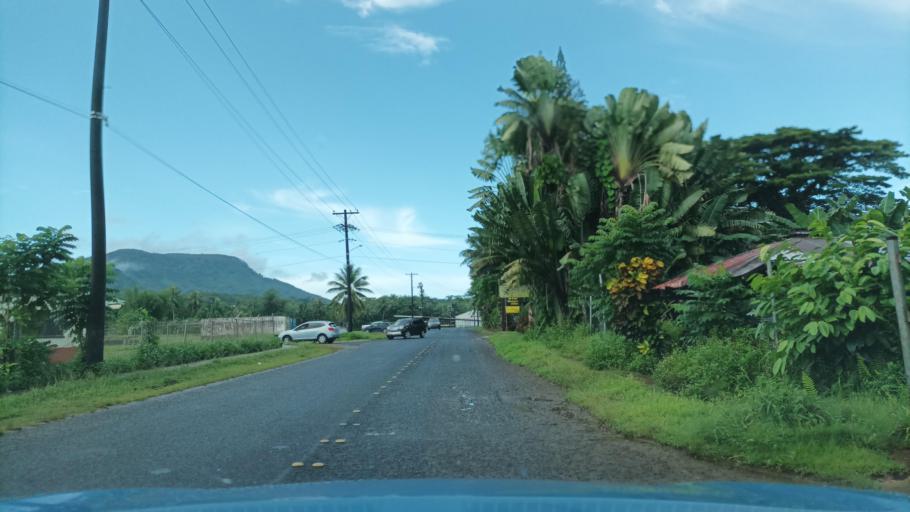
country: FM
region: Pohnpei
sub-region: Kolonia Municipality
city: Kolonia Town
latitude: 6.9516
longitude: 158.2061
